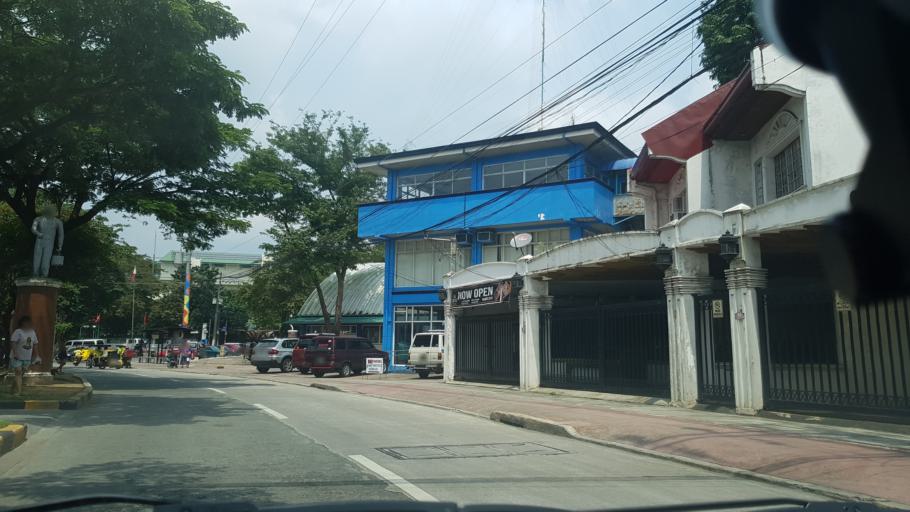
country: PH
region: Calabarzon
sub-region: Province of Rizal
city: Antipolo
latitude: 14.6493
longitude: 121.1172
